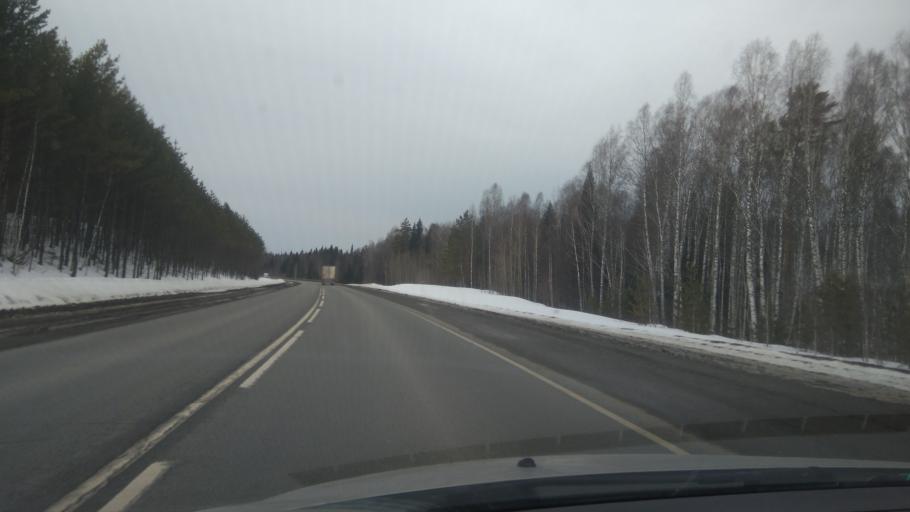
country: RU
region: Sverdlovsk
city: Ufimskiy
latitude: 56.7859
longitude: 58.3895
